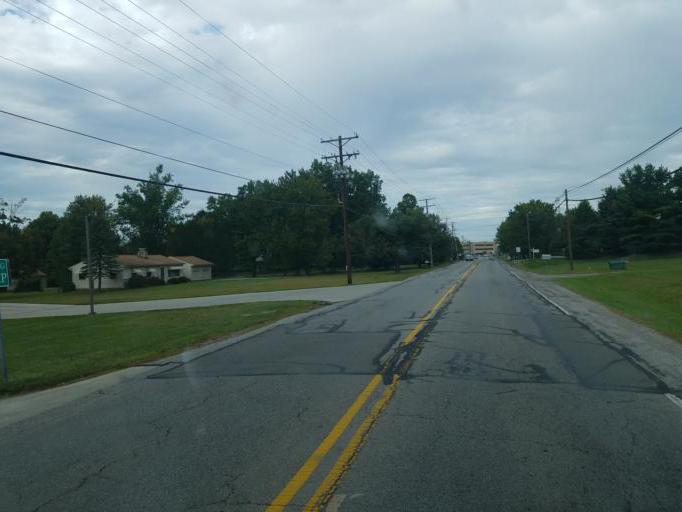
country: US
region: Ohio
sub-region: Franklin County
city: Reynoldsburg
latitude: 39.9756
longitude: -82.8366
